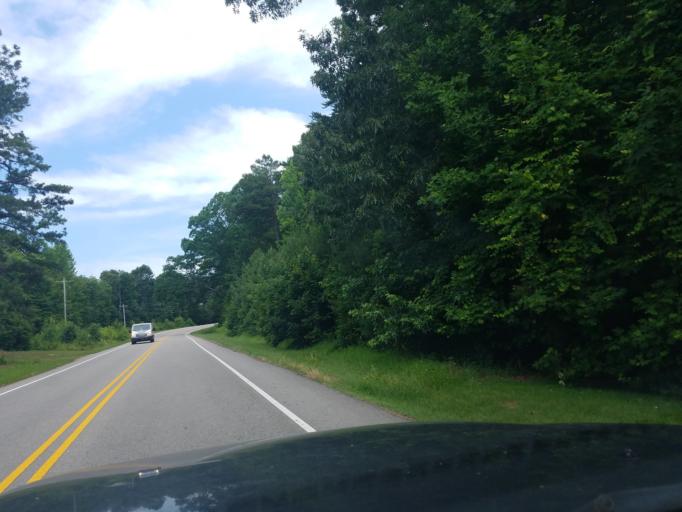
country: US
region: North Carolina
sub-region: Durham County
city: Durham
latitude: 36.1207
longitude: -78.9347
